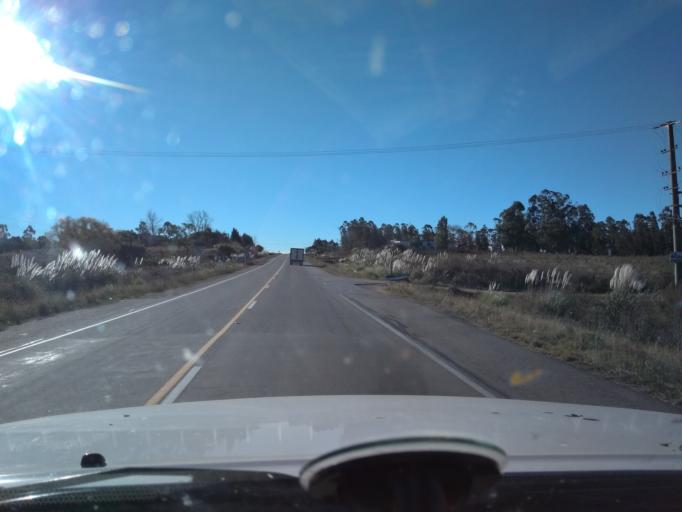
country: UY
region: Canelones
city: Sauce
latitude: -34.5938
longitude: -56.0519
